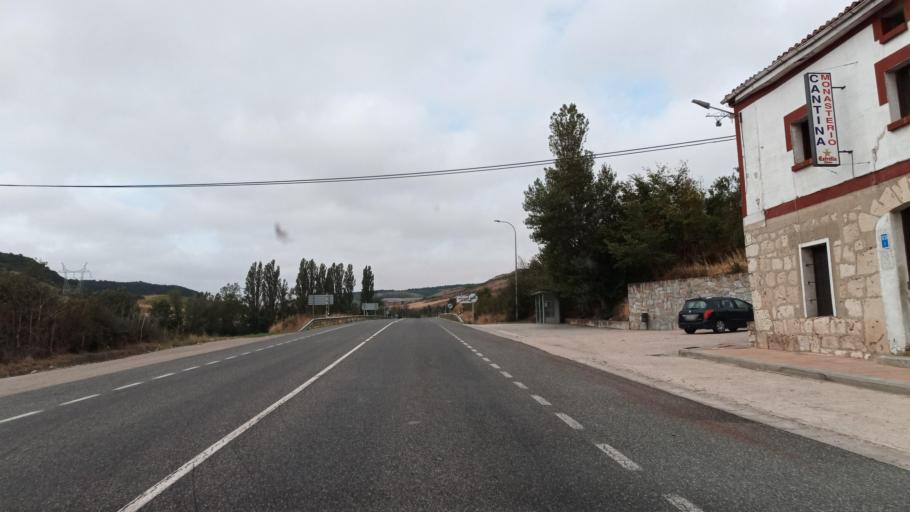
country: ES
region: Castille and Leon
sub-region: Provincia de Burgos
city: Monasterio de Rodilla
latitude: 42.4567
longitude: -3.4691
